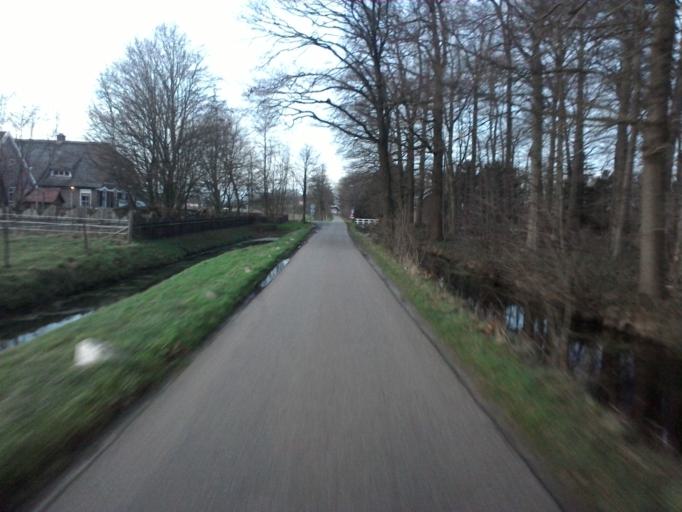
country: NL
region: Utrecht
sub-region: Gemeente De Bilt
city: De Bilt
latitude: 52.0888
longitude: 5.1885
